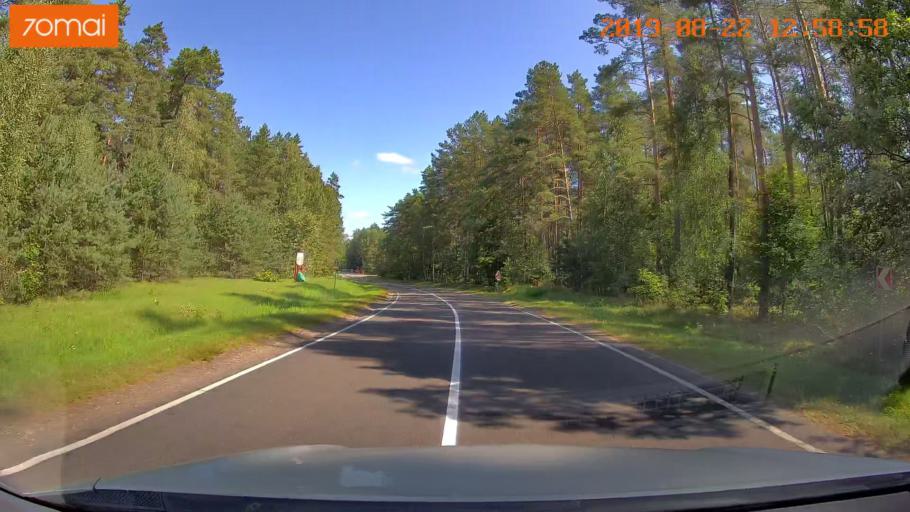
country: BY
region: Minsk
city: Prawdzinski
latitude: 53.4220
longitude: 27.7825
